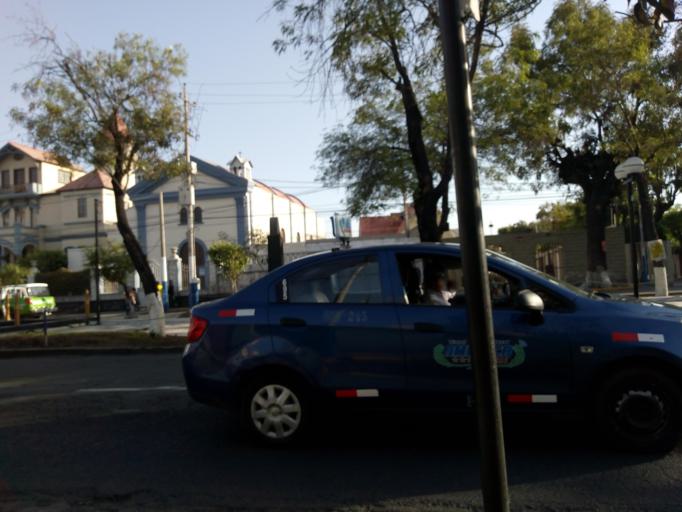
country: PE
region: Arequipa
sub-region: Provincia de Arequipa
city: Arequipa
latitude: -16.3917
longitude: -71.5417
